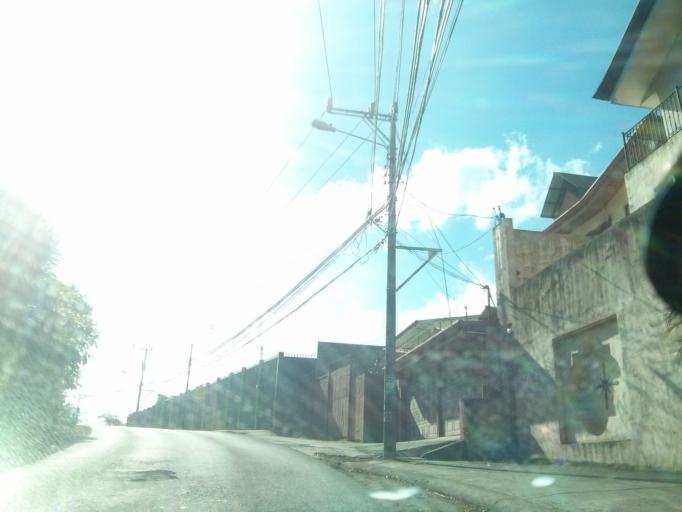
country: CR
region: San Jose
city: Granadilla
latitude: 9.9303
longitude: -84.0282
